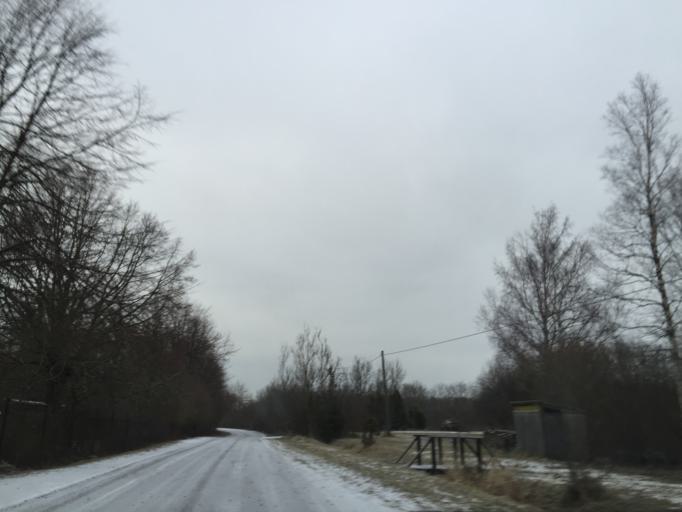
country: EE
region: Saare
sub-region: Orissaare vald
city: Orissaare
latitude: 58.6769
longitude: 23.1970
